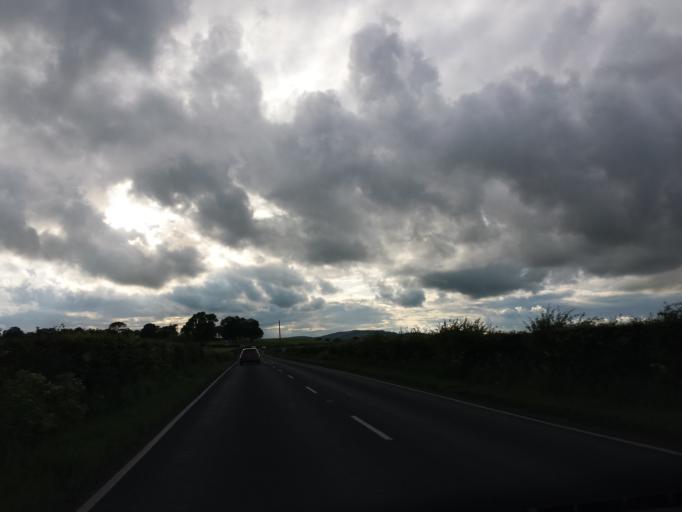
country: GB
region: Scotland
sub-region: Fife
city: Strathkinness
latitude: 56.3530
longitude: -2.8495
